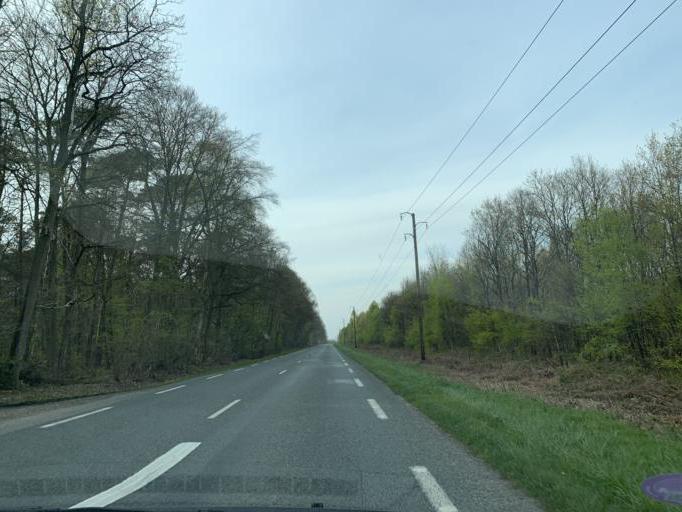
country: FR
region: Haute-Normandie
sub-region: Departement de la Seine-Maritime
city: Jumieges
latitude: 49.4198
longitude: 0.7948
